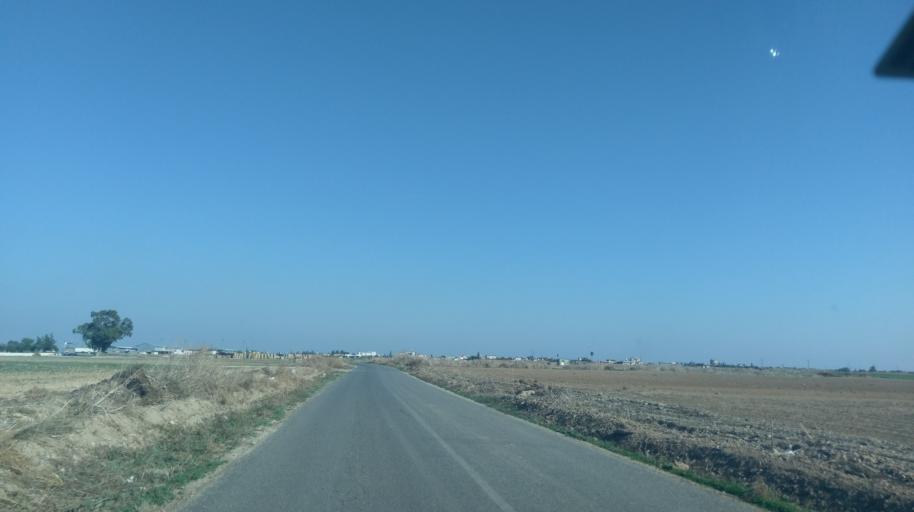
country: CY
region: Larnaka
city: Pergamos
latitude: 35.1035
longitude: 33.6650
